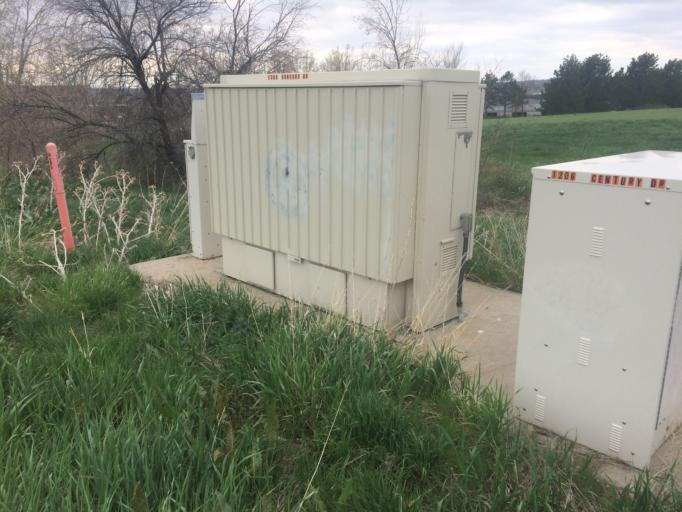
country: US
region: Colorado
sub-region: Boulder County
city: Superior
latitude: 39.9695
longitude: -105.1704
